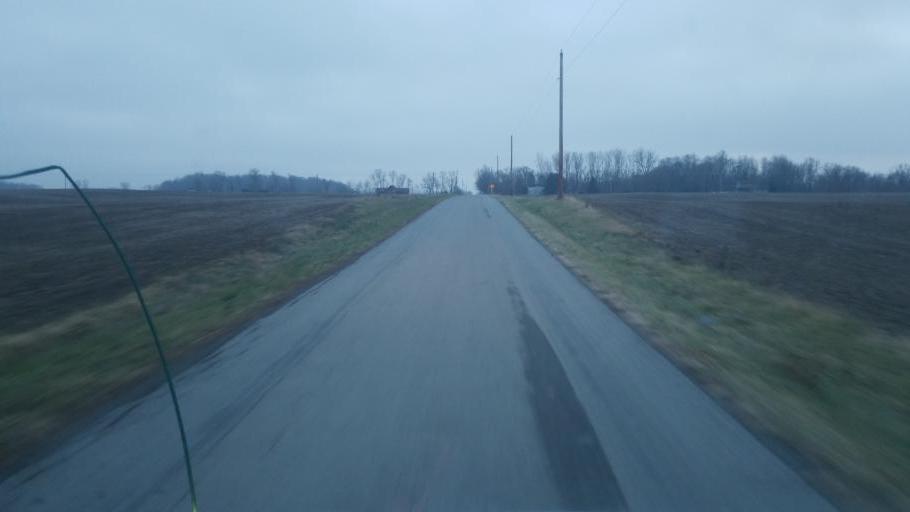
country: US
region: Ohio
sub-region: Seneca County
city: Tiffin
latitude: 40.9675
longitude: -83.1318
